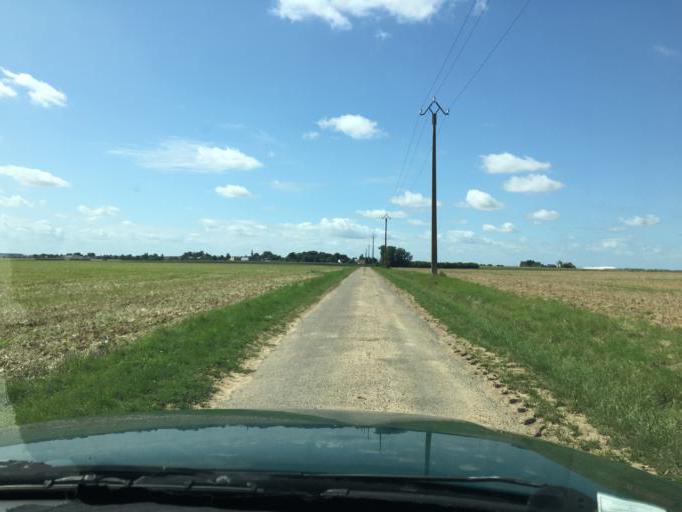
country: FR
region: Centre
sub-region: Departement du Loiret
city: Patay
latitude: 48.0124
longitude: 1.7106
